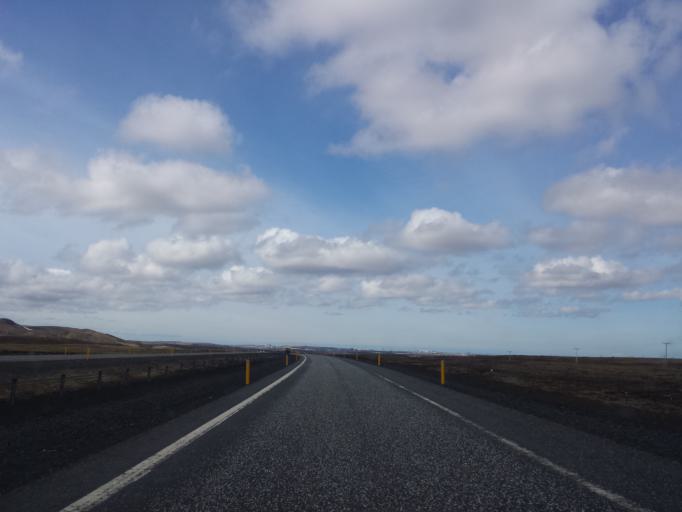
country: IS
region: Capital Region
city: Mosfellsbaer
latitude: 64.0707
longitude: -21.6112
